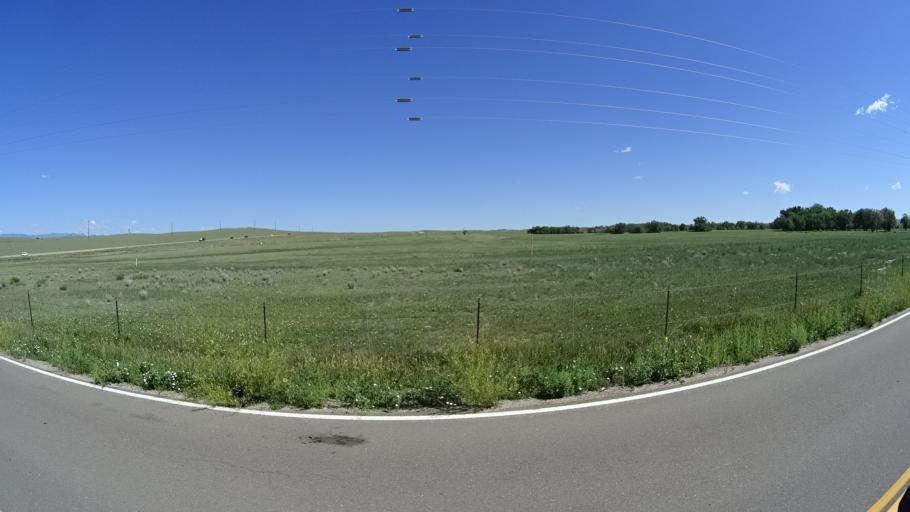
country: US
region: Colorado
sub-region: El Paso County
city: Security-Widefield
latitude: 38.7809
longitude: -104.6567
